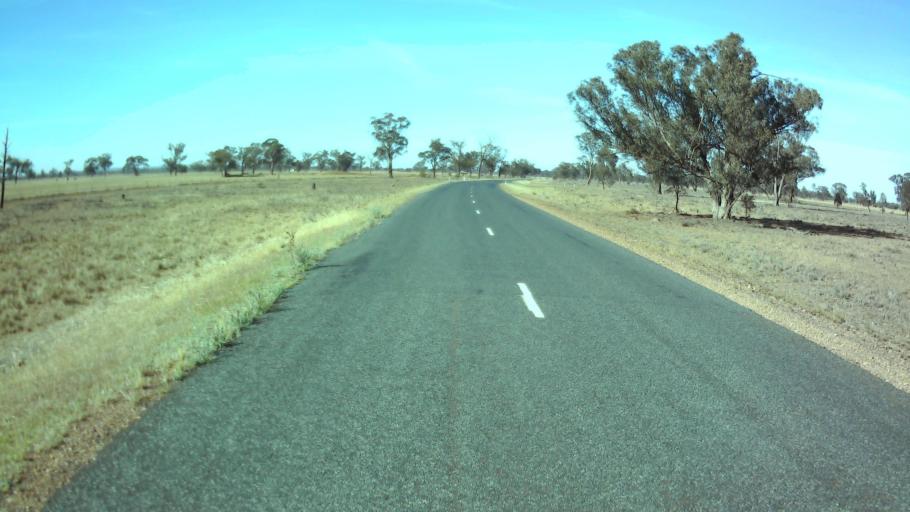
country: AU
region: New South Wales
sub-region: Weddin
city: Grenfell
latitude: -34.0687
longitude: 147.9053
